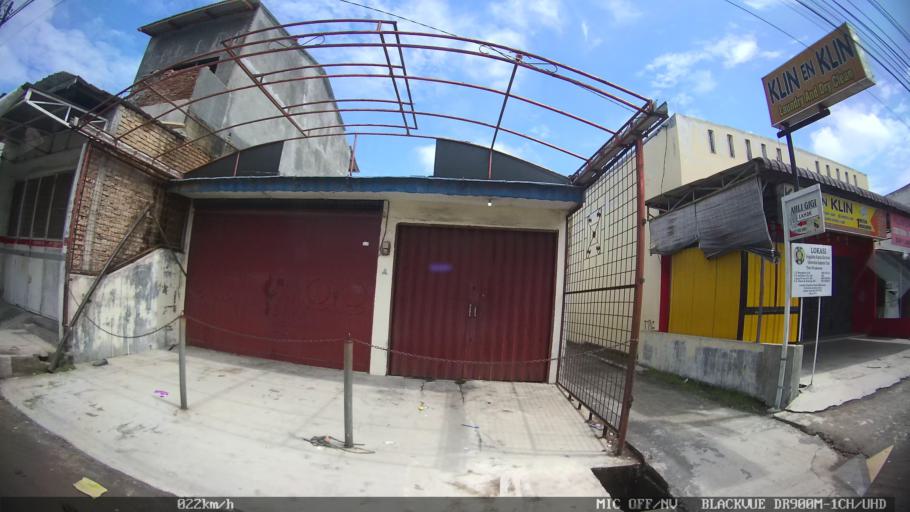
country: ID
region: North Sumatra
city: Medan
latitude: 3.5910
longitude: 98.7492
